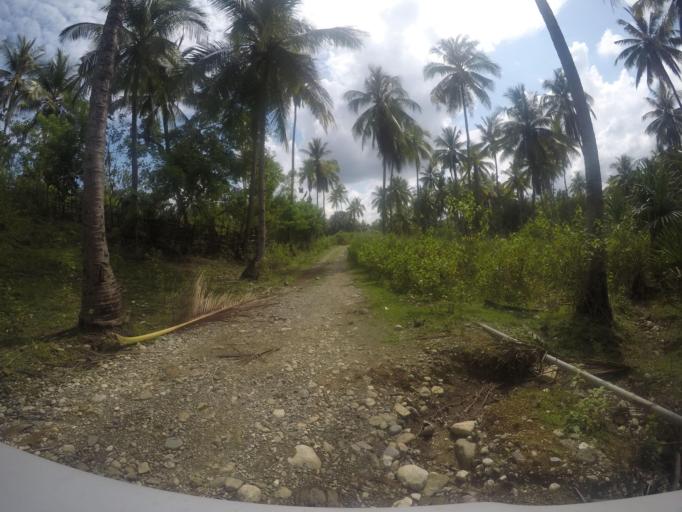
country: TL
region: Viqueque
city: Viqueque
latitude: -8.8499
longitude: 126.3616
